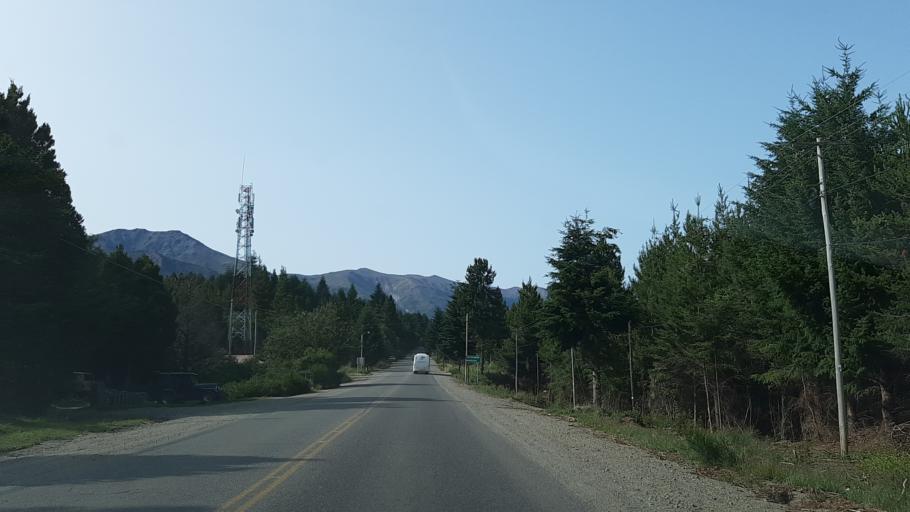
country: AR
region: Rio Negro
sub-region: Departamento de Bariloche
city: San Carlos de Bariloche
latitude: -41.1524
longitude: -71.4086
